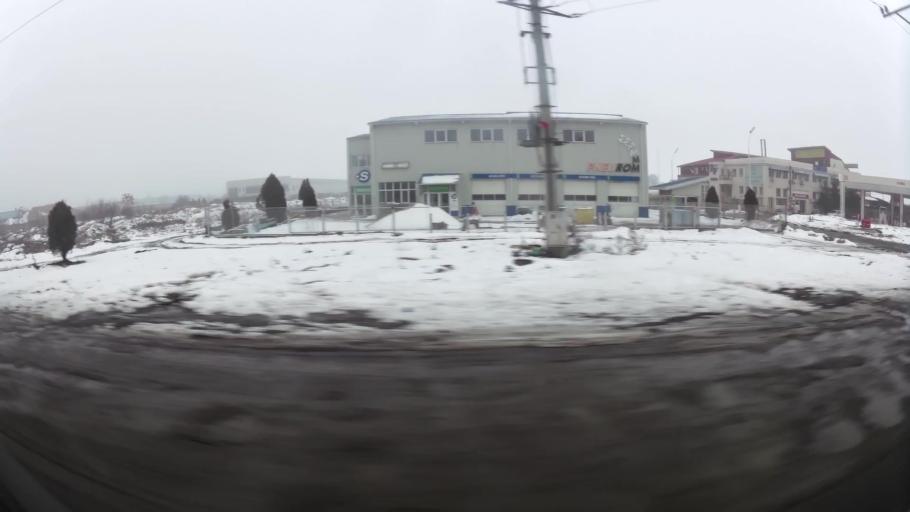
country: RO
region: Ilfov
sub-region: Comuna Clinceni
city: Olteni
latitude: 44.4105
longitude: 25.9738
